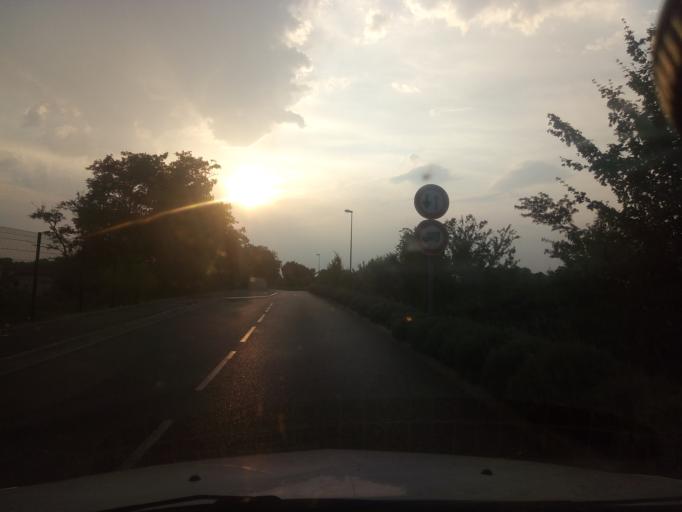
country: FR
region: Rhone-Alpes
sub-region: Departement du Rhone
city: Saint-Laurent-de-Mure
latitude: 45.6936
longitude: 5.0455
